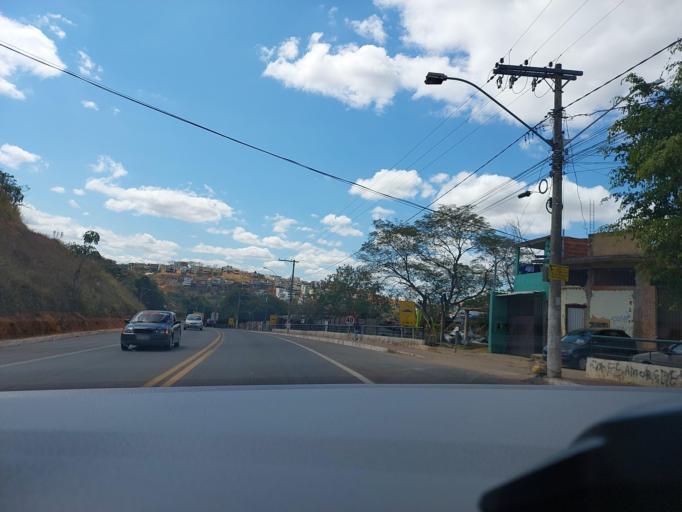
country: BR
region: Minas Gerais
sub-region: Muriae
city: Muriae
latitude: -21.1288
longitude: -42.3585
